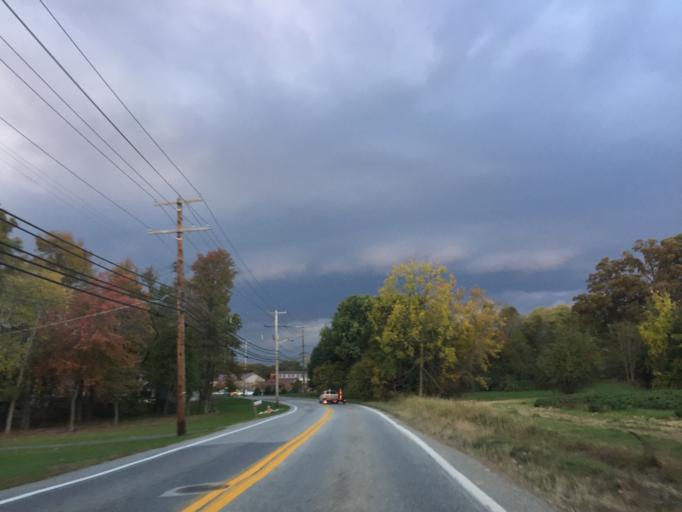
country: US
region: Maryland
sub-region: Baltimore County
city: White Marsh
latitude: 39.3745
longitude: -76.4151
